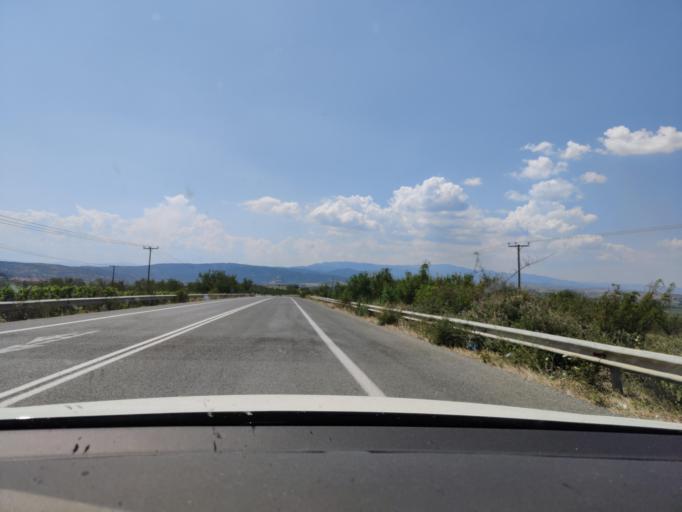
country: GR
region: Central Macedonia
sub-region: Nomos Serron
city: Palaiokomi
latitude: 40.8631
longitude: 23.8623
